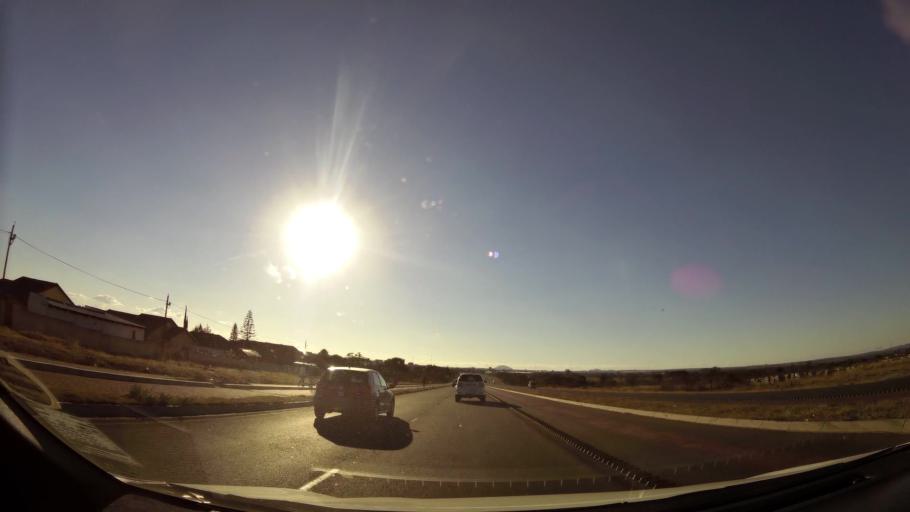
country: ZA
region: Limpopo
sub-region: Capricorn District Municipality
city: Polokwane
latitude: -23.8603
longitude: 29.4045
